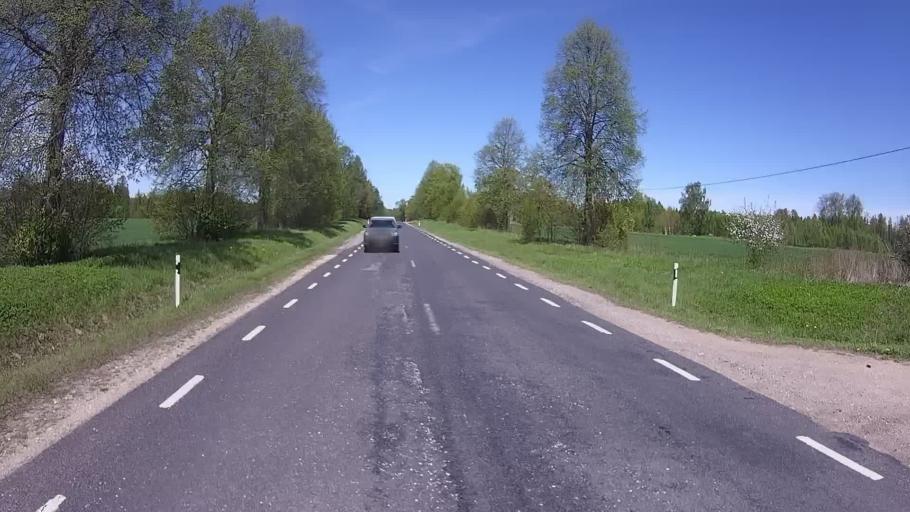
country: EE
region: Polvamaa
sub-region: Raepina vald
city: Rapina
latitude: 58.0413
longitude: 27.3922
